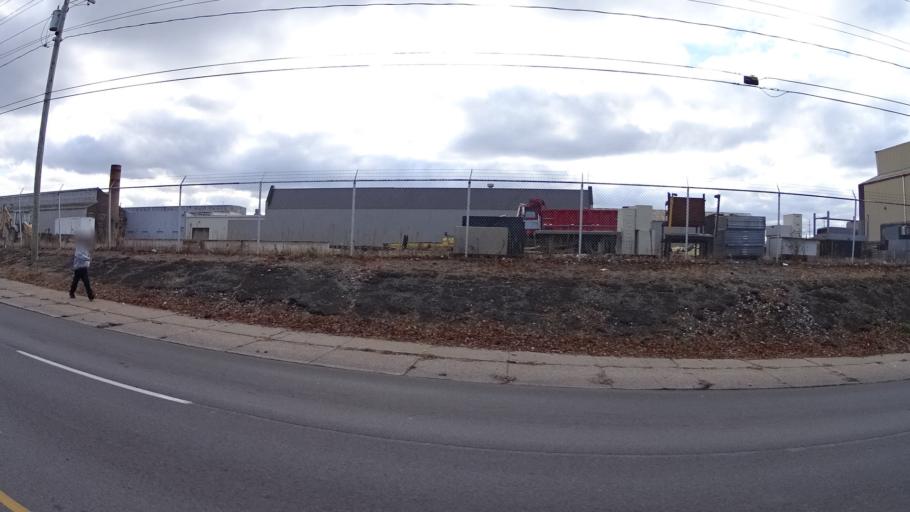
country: US
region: Ohio
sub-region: Lorain County
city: Lorain
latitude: 41.4452
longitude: -82.1541
